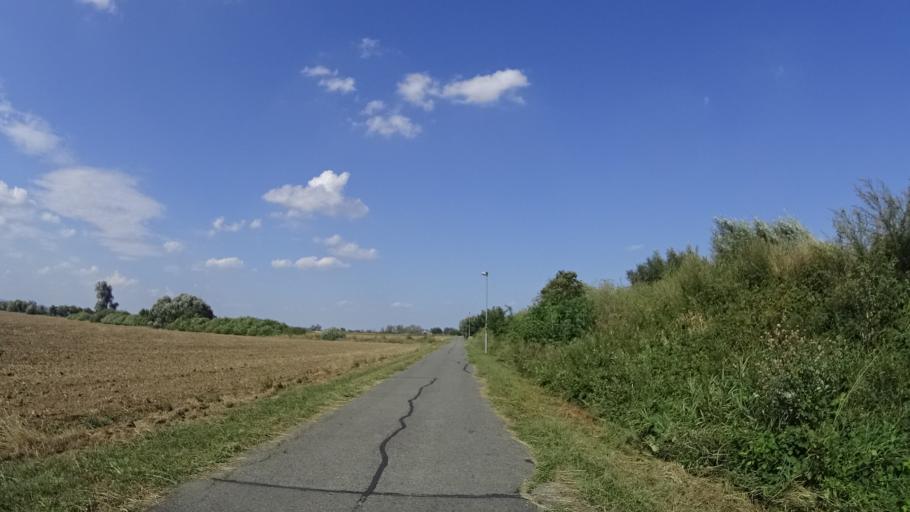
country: CZ
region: Zlin
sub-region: Okres Zlin
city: Ostrozska Nova Ves
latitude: 48.9948
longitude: 17.4192
